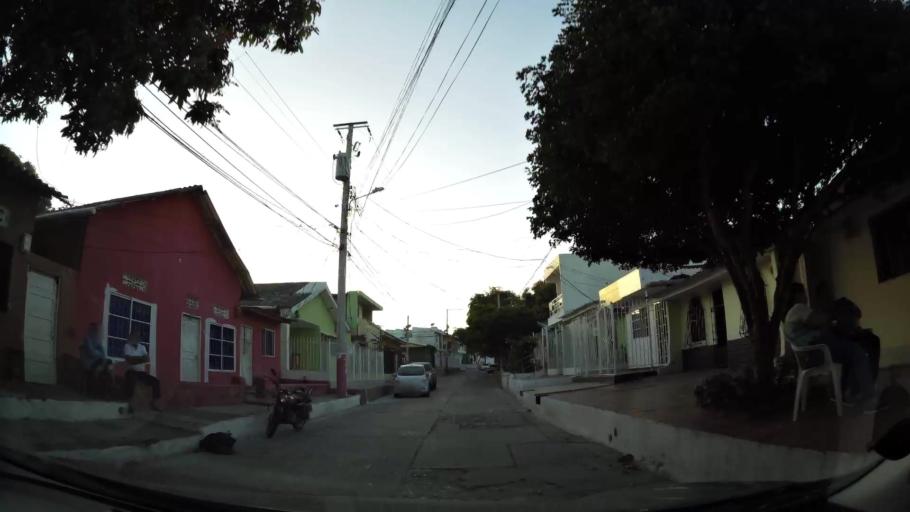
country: CO
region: Atlantico
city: Barranquilla
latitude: 10.9738
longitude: -74.8067
